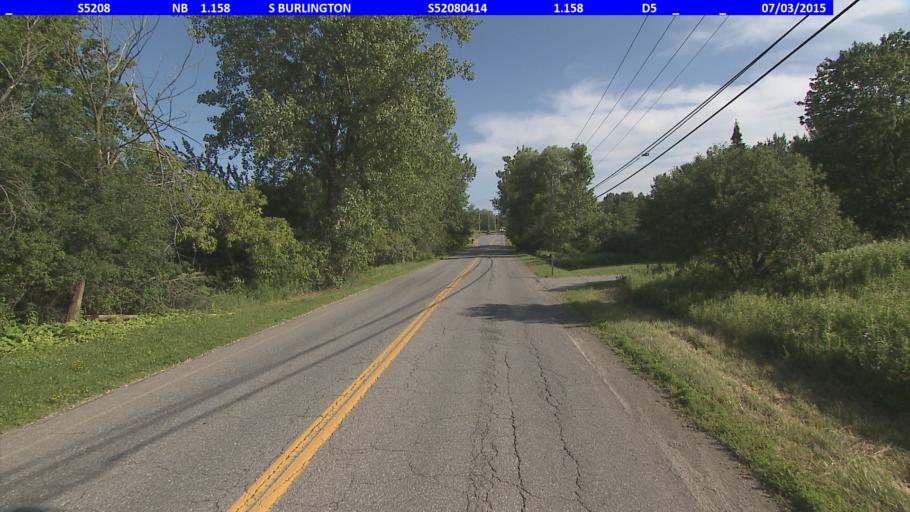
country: US
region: Vermont
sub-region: Chittenden County
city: South Burlington
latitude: 44.4274
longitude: -73.1745
